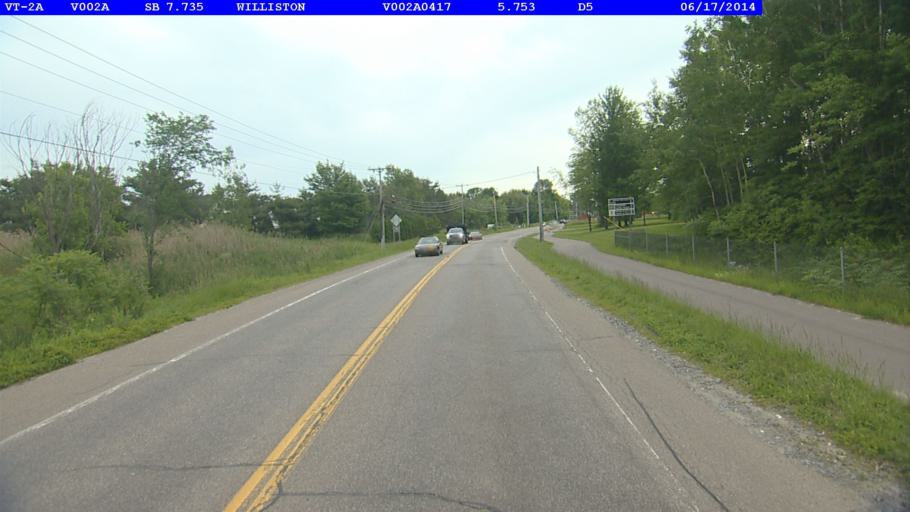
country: US
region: Vermont
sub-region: Chittenden County
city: Essex Junction
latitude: 44.4789
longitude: -73.1141
